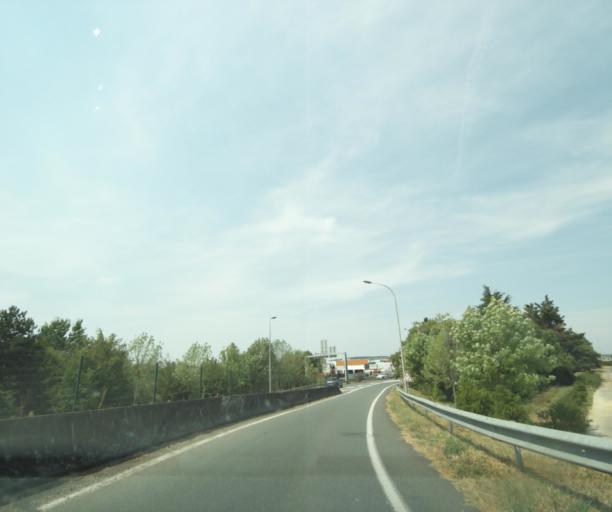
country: FR
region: Poitou-Charentes
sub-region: Departement de la Vienne
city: Antran
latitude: 46.8383
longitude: 0.5477
